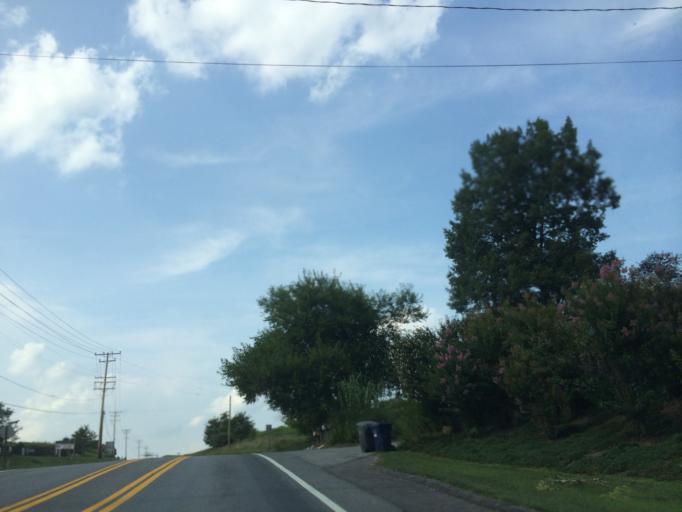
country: US
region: Maryland
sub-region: Carroll County
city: Sykesville
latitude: 39.3542
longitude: -77.0157
